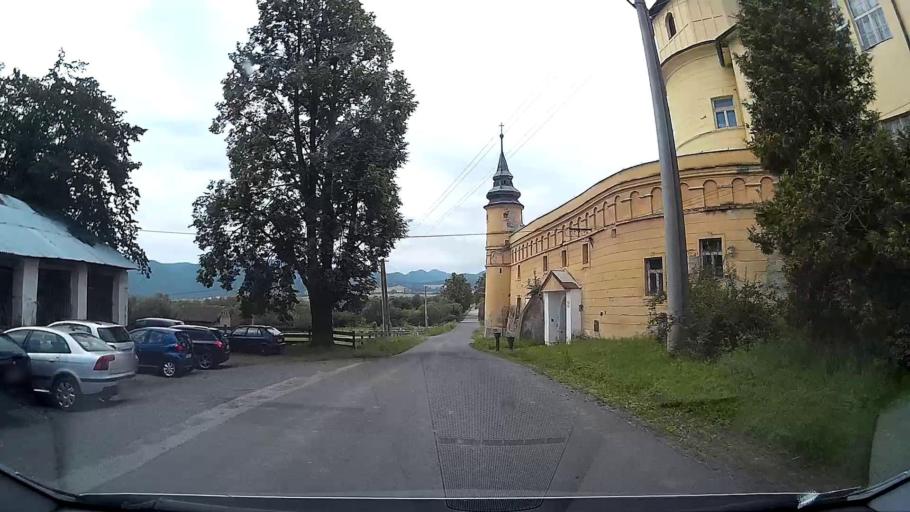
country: SK
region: Presovsky
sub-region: Okres Poprad
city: Poprad
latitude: 48.9889
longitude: 20.3810
